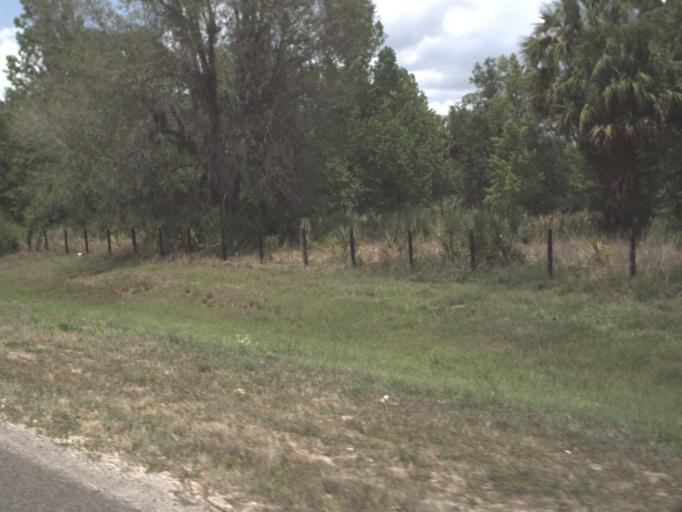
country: US
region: Florida
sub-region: Sumter County
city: Lake Panasoffkee
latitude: 28.8583
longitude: -82.1800
